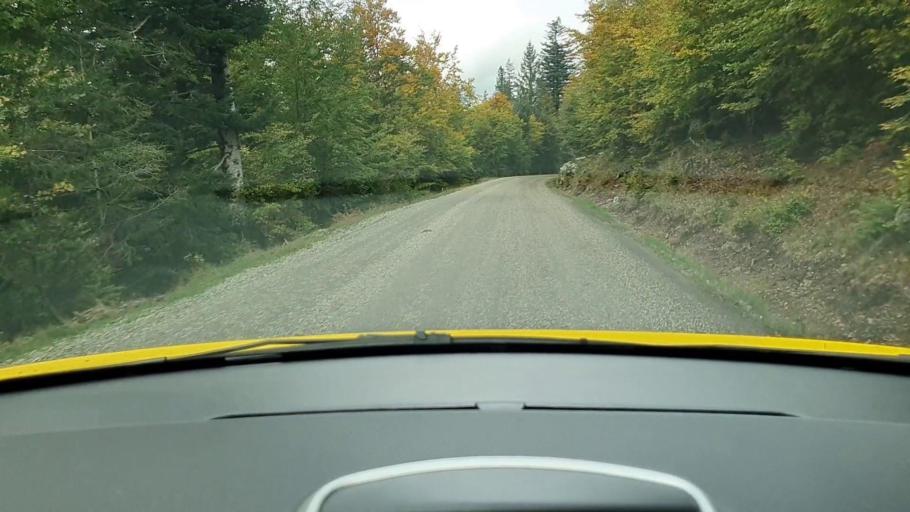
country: FR
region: Languedoc-Roussillon
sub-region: Departement du Gard
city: Le Vigan
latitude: 44.0565
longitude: 3.5467
